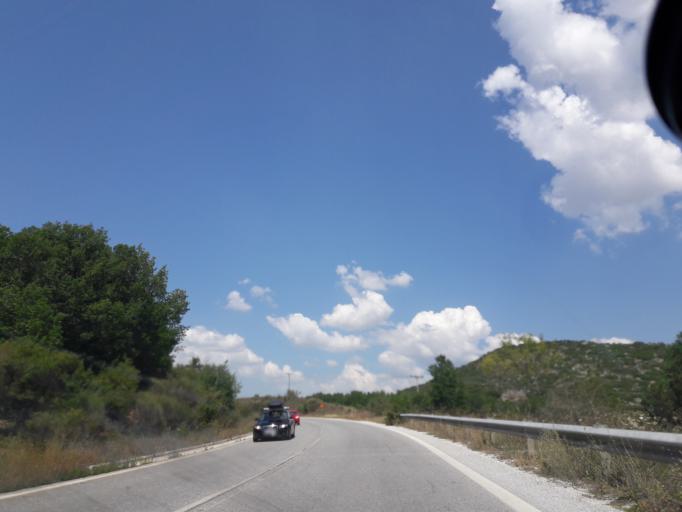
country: GR
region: Central Macedonia
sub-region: Nomos Chalkidikis
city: Polygyros
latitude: 40.4537
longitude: 23.4129
